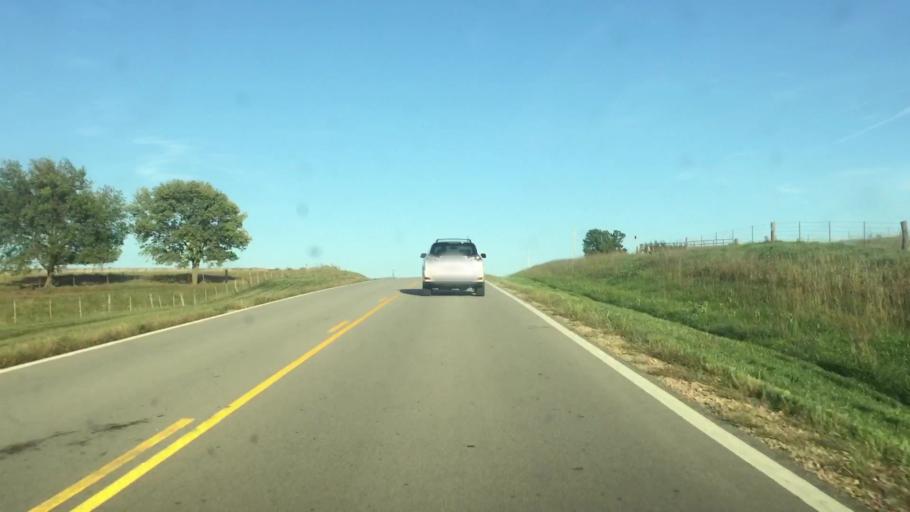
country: US
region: Kansas
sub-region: Brown County
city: Horton
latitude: 39.5874
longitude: -95.5476
